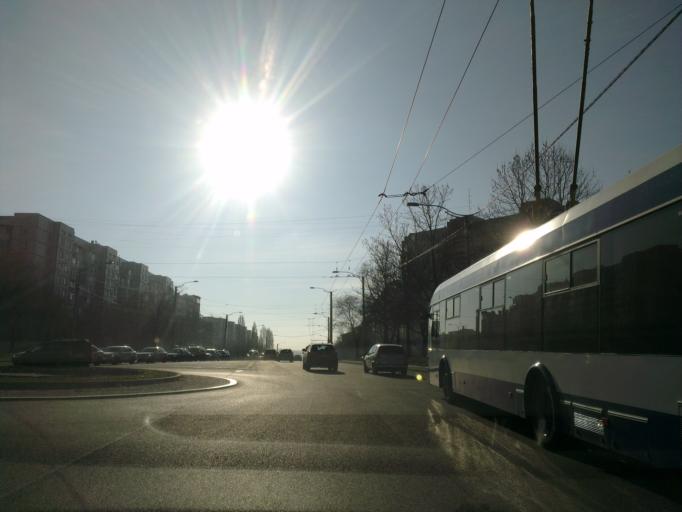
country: MD
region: Chisinau
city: Chisinau
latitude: 47.0394
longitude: 28.8819
